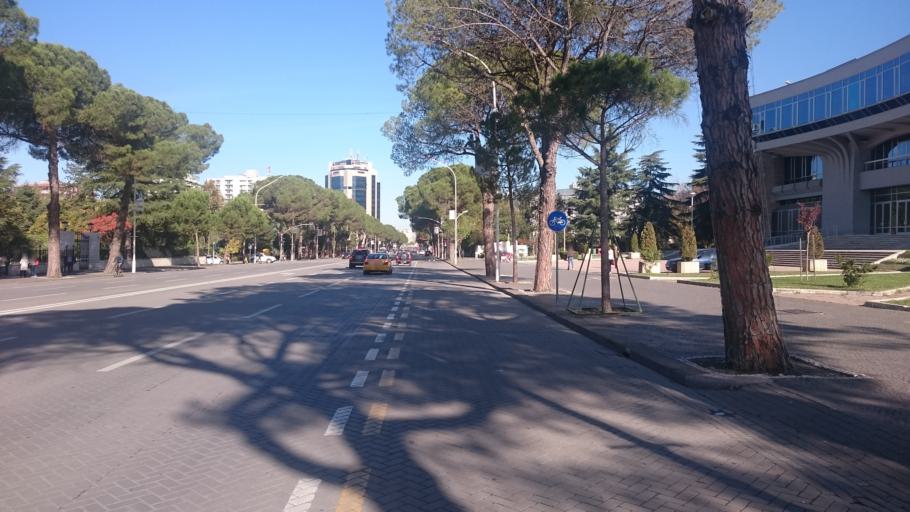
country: AL
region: Tirane
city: Tirana
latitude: 41.3186
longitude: 19.8212
